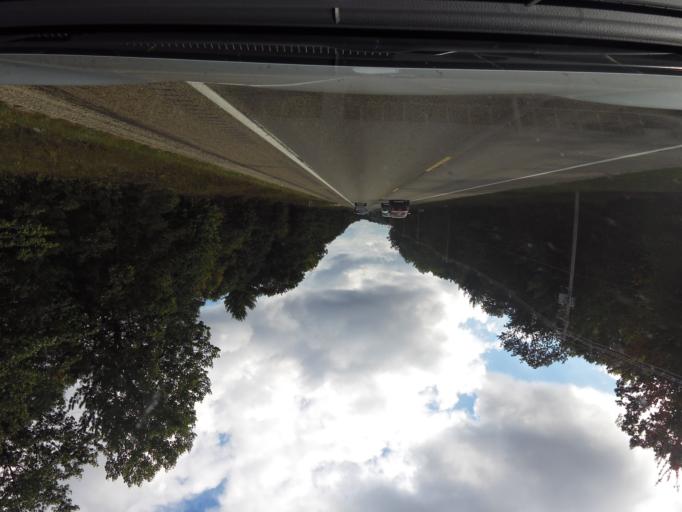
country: US
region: Michigan
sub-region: Roscommon County
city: Prudenville
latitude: 44.3055
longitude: -84.6223
